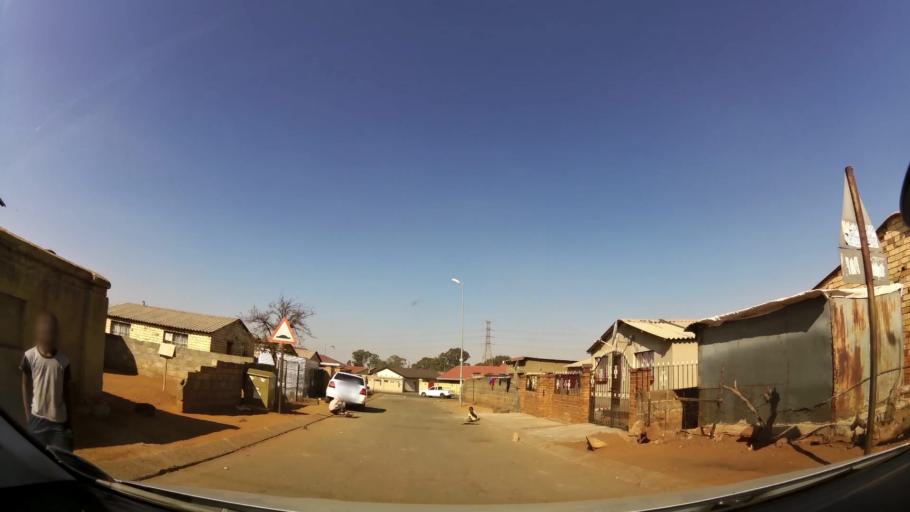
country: ZA
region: Gauteng
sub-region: City of Johannesburg Metropolitan Municipality
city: Soweto
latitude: -26.2864
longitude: 27.8690
